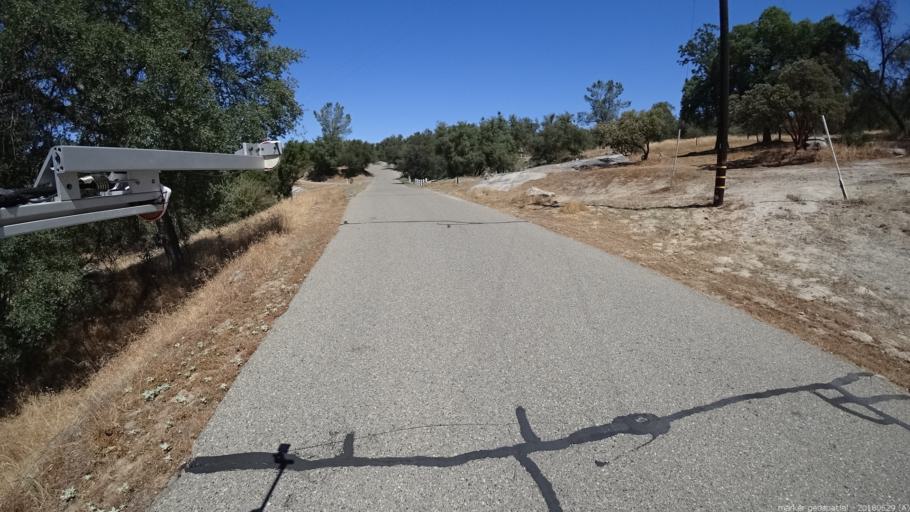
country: US
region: California
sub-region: Madera County
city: Yosemite Lakes
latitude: 37.1612
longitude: -119.7552
